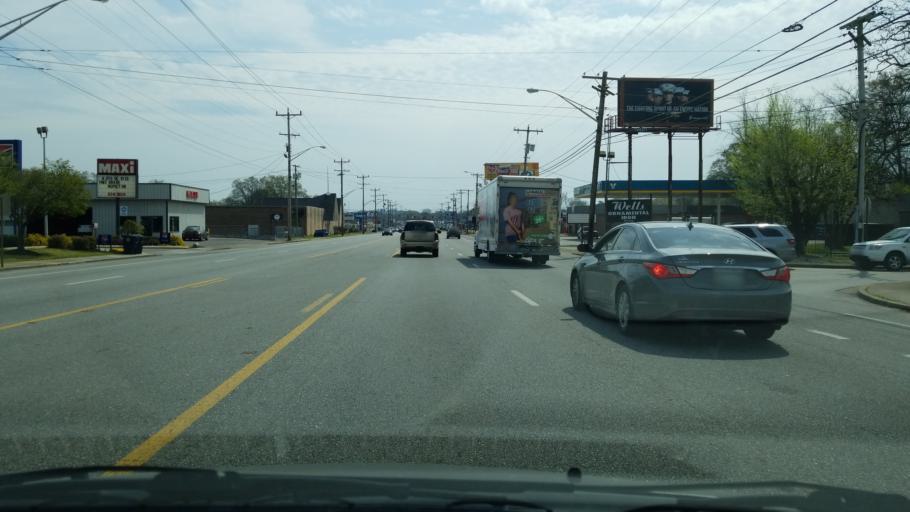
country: US
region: Tennessee
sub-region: Hamilton County
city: East Ridge
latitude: 34.9940
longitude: -85.2314
